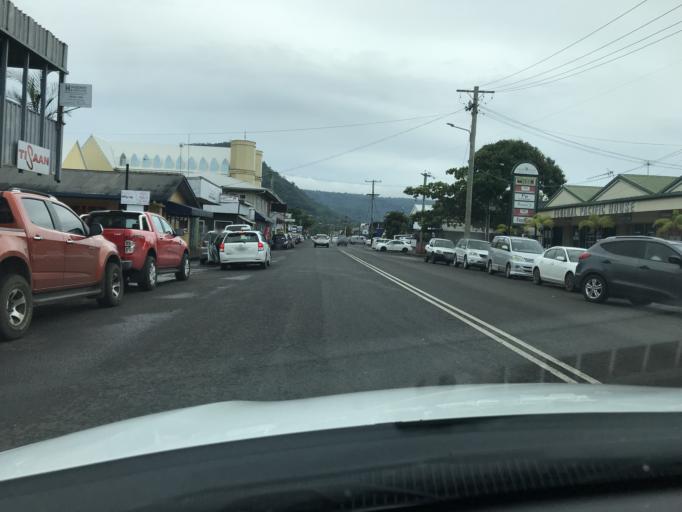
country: WS
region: Tuamasaga
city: Apia
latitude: -13.8329
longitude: -171.7694
